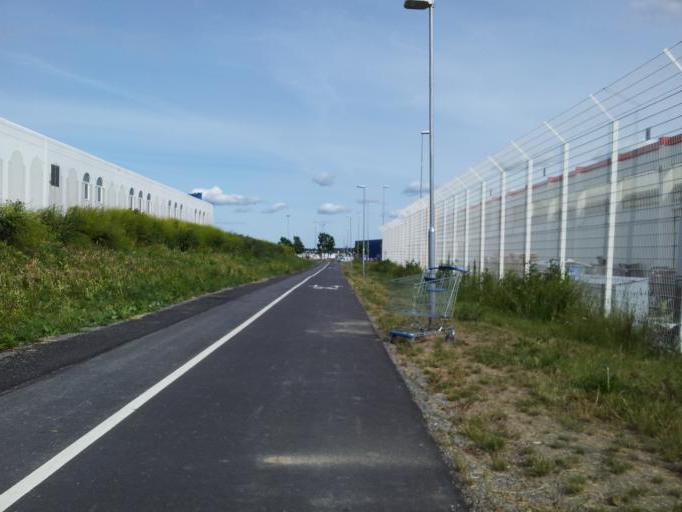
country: SE
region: Uppsala
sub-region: Uppsala Kommun
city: Saevja
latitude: 59.8495
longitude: 17.6882
